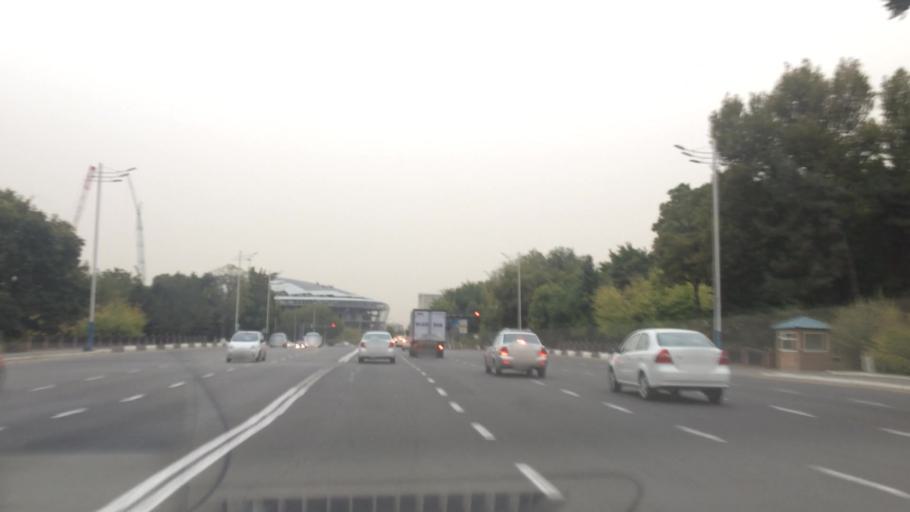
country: UZ
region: Toshkent Shahri
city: Tashkent
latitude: 41.3073
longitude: 69.2578
